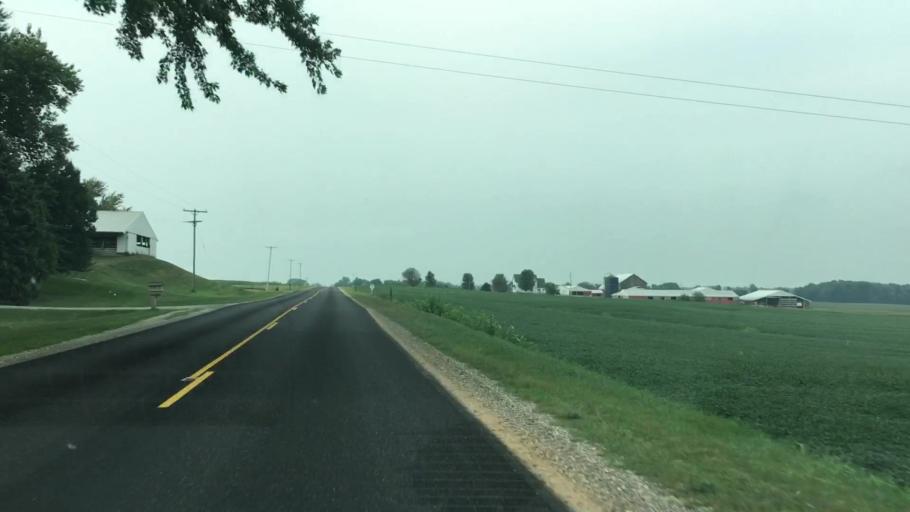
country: US
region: Michigan
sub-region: Ottawa County
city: Hudsonville
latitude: 42.7976
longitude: -85.9008
